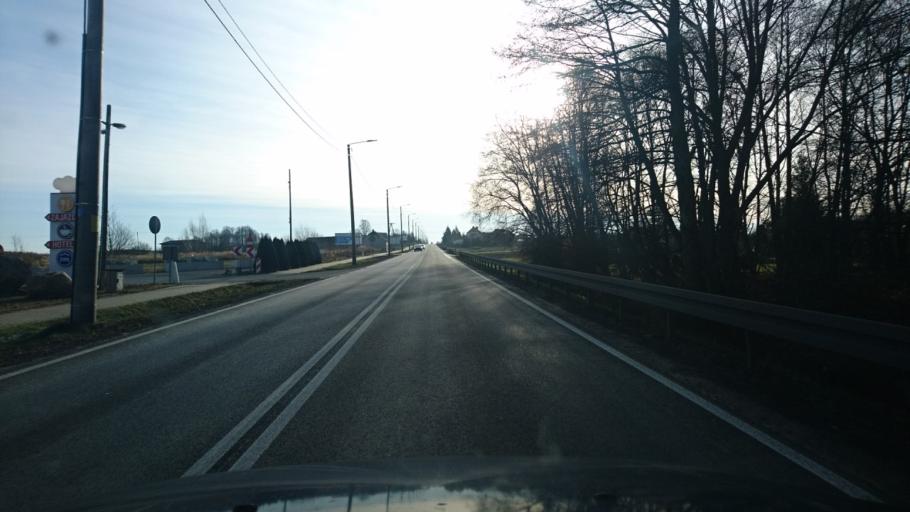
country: PL
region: Greater Poland Voivodeship
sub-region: Powiat ostrzeszowski
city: Ostrzeszow
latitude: 51.4134
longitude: 17.9330
